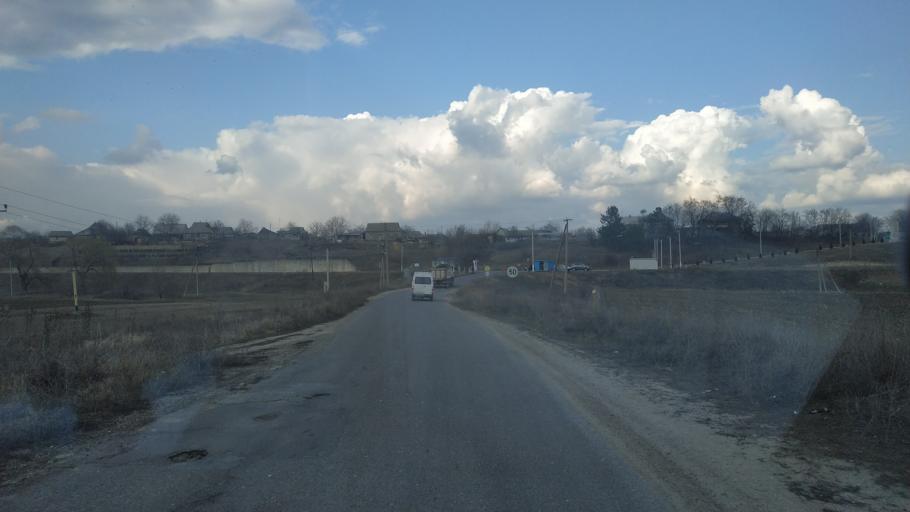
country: MD
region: Anenii Noi
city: Varnita
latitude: 46.9194
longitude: 29.4546
